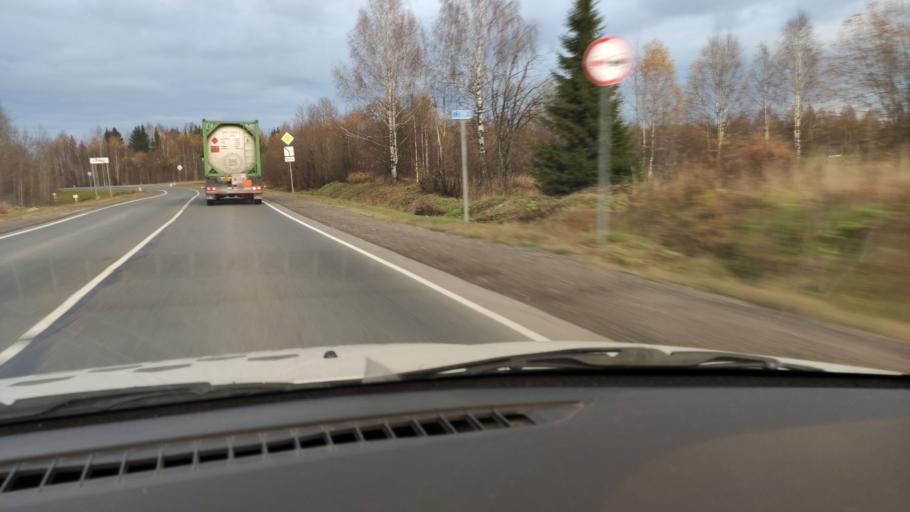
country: RU
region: Kirov
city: Belorechensk
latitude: 58.7165
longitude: 52.3323
